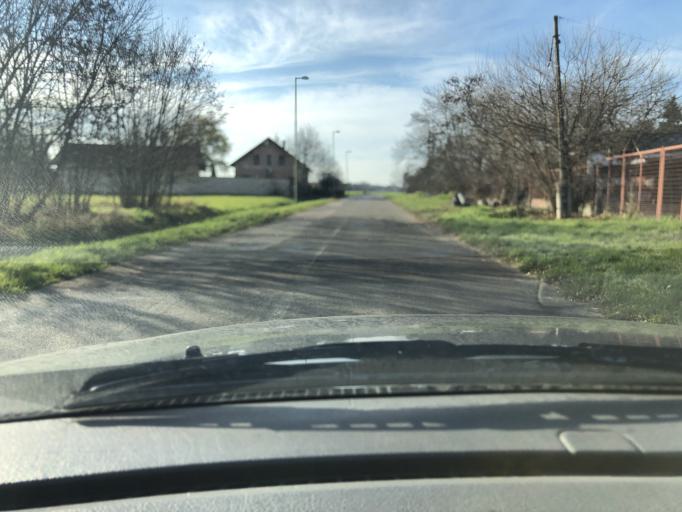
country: HU
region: Csongrad
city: Csongrad
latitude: 46.7129
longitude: 20.1766
